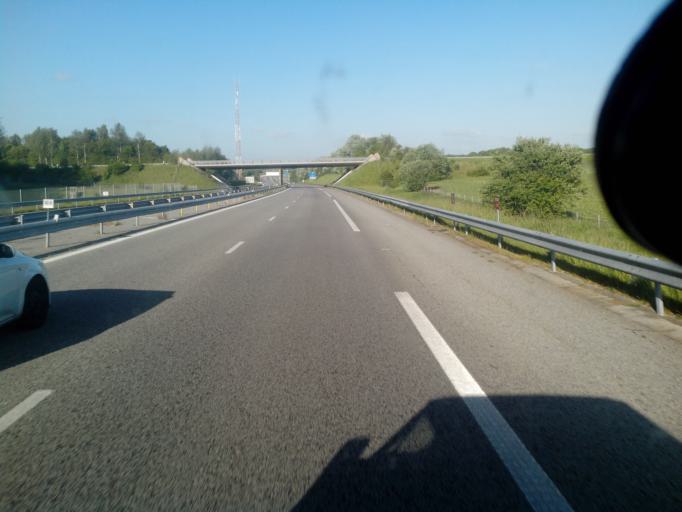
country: FR
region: Haute-Normandie
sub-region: Departement de la Seine-Maritime
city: Valliquerville
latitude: 49.6357
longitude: 0.6767
